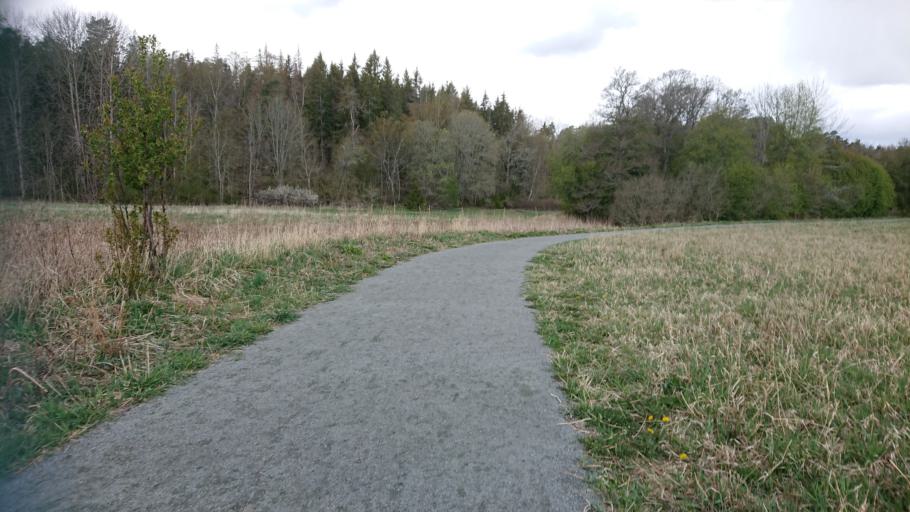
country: SE
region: Uppsala
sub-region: Uppsala Kommun
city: Uppsala
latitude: 59.7980
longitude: 17.6084
